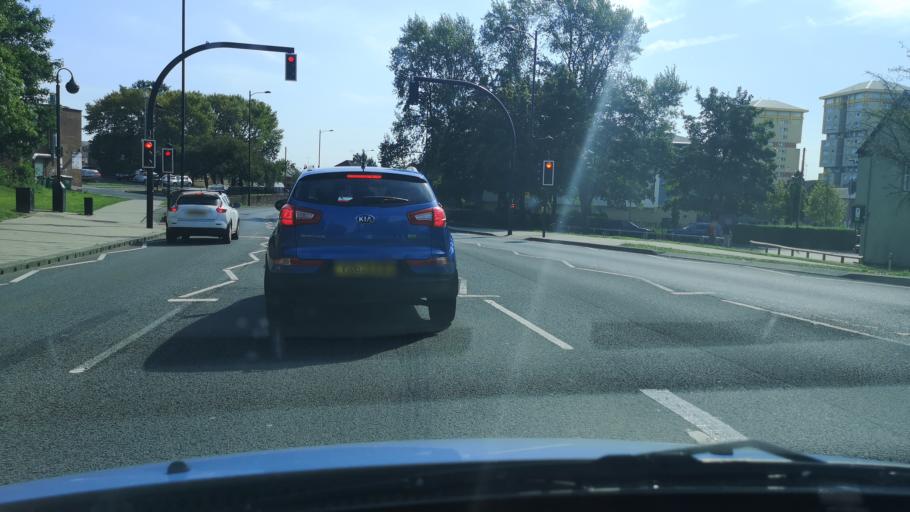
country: GB
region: England
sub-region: City and Borough of Wakefield
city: Wakefield
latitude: 53.6839
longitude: -1.4925
